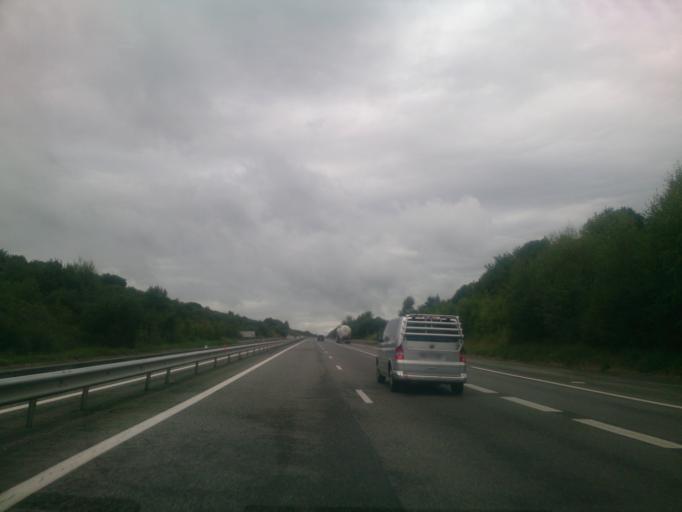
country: FR
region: Midi-Pyrenees
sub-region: Departement de la Haute-Garonne
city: Montrejeau
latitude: 43.0959
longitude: 0.5521
